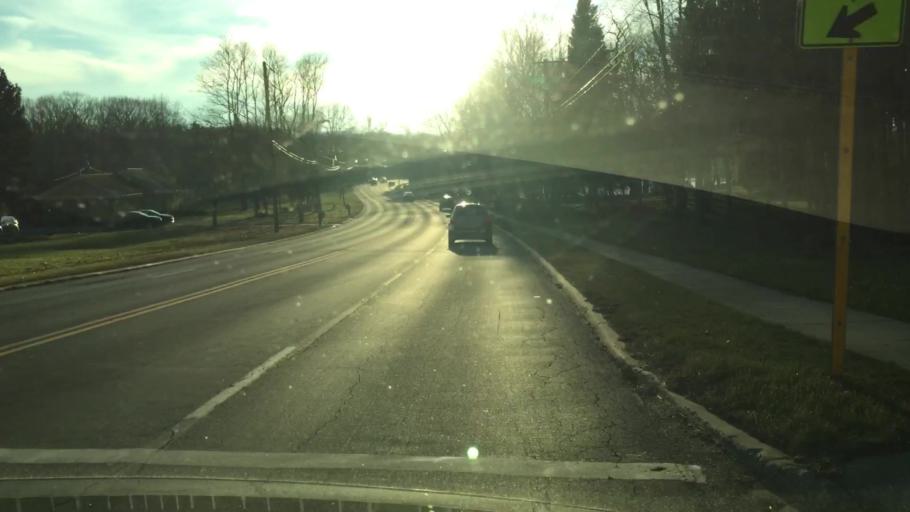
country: US
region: Ohio
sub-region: Summit County
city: Silver Lake
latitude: 41.1541
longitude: -81.4529
